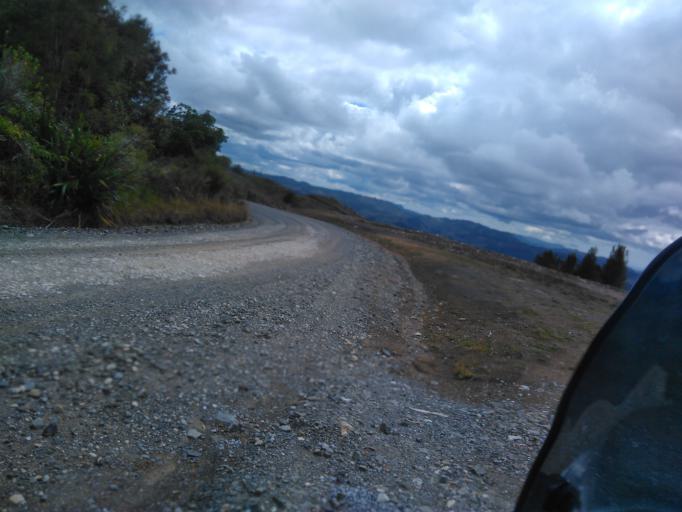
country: NZ
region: Gisborne
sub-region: Gisborne District
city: Gisborne
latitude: -38.2440
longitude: 178.0687
